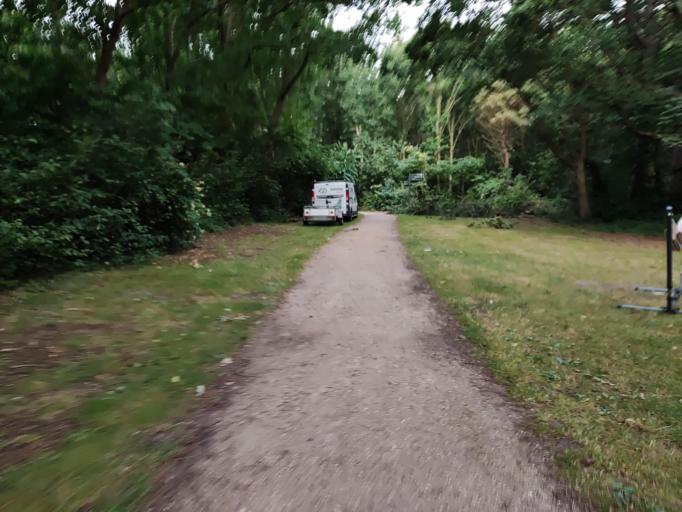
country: NL
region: North Holland
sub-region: Gemeente Texel
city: Den Burg
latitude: 53.0890
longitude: 4.7686
